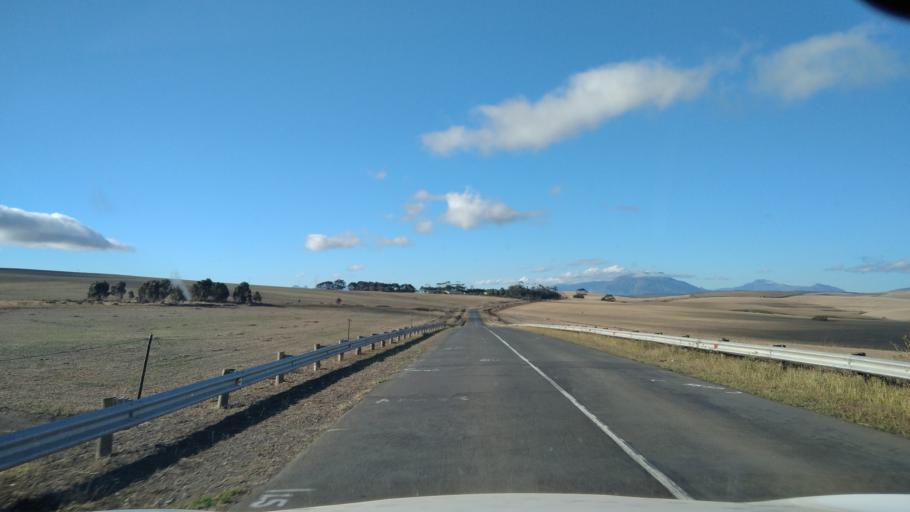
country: ZA
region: Western Cape
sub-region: Overberg District Municipality
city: Caledon
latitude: -34.2113
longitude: 19.2725
